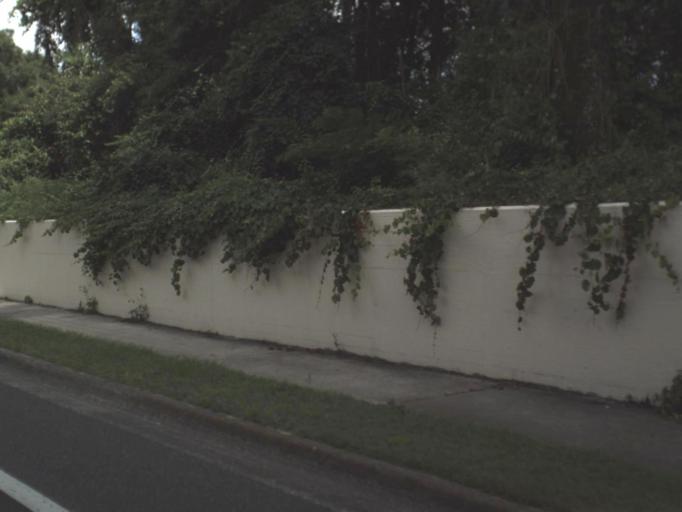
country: US
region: Florida
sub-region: Alachua County
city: Alachua
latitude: 29.6887
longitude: -82.4177
